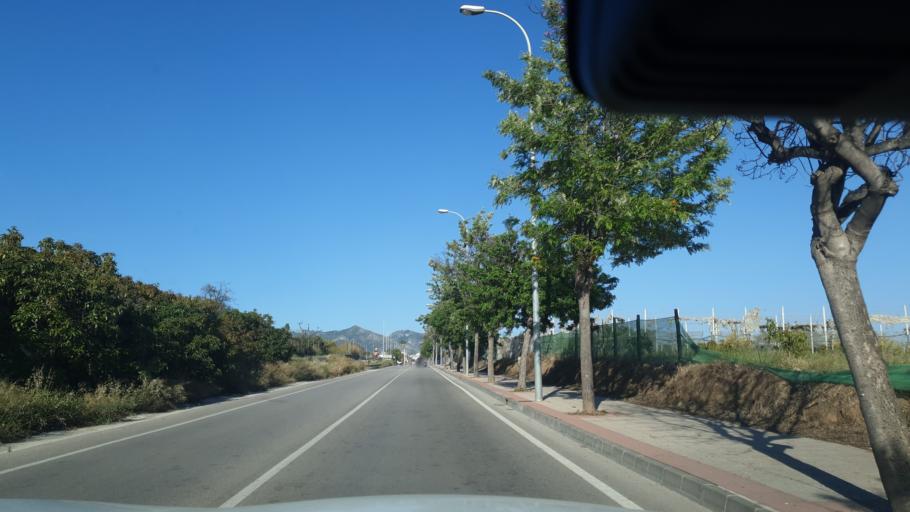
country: ES
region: Andalusia
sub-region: Provincia de Malaga
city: Nerja
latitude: 36.7461
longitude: -3.8948
